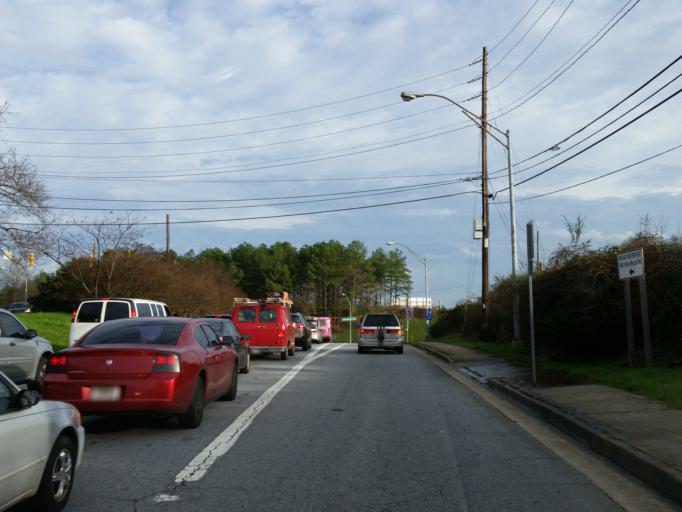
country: US
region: Georgia
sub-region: DeKalb County
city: North Druid Hills
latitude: 33.8244
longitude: -84.3574
